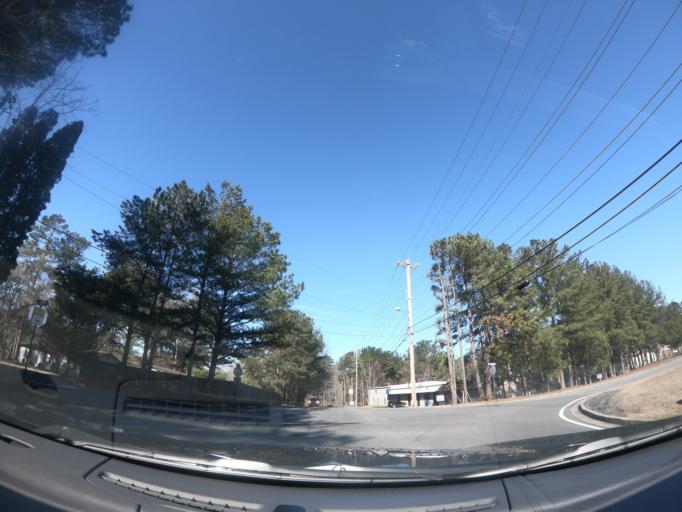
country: US
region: Georgia
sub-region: Cobb County
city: Acworth
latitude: 34.0583
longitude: -84.6614
